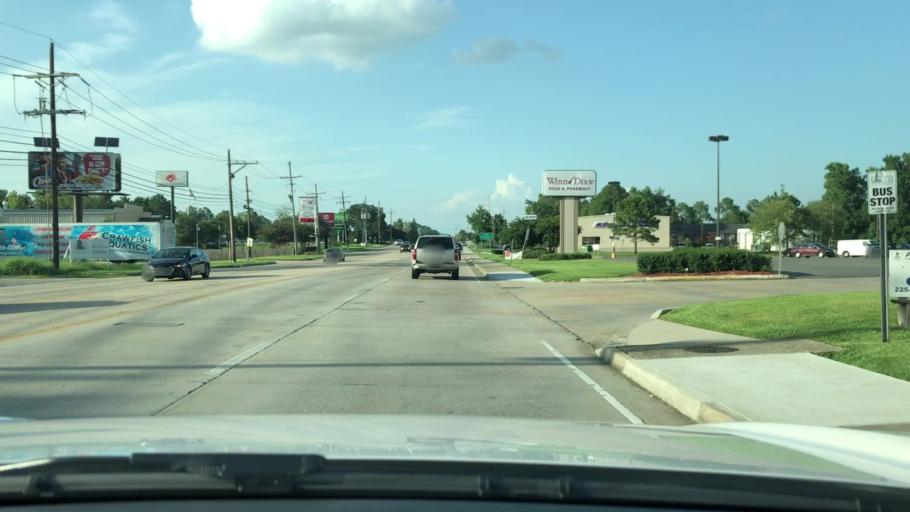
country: US
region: Louisiana
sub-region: East Baton Rouge Parish
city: Village Saint George
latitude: 30.3701
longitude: -91.0733
